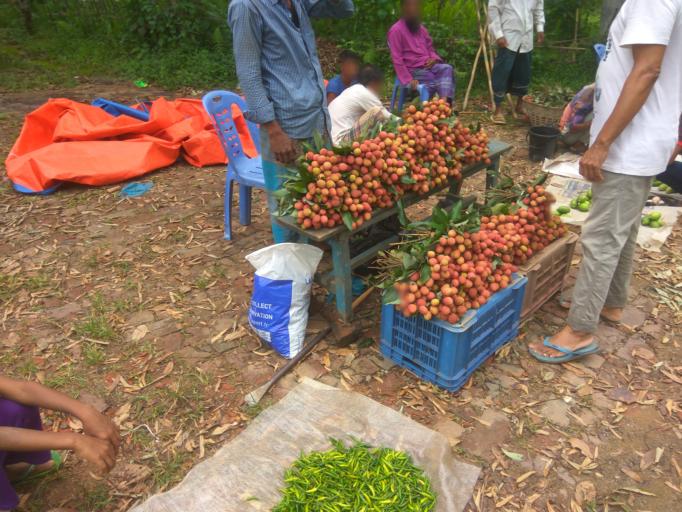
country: IN
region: Assam
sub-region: Karimganj
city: Karimganj
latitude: 24.7880
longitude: 92.1721
